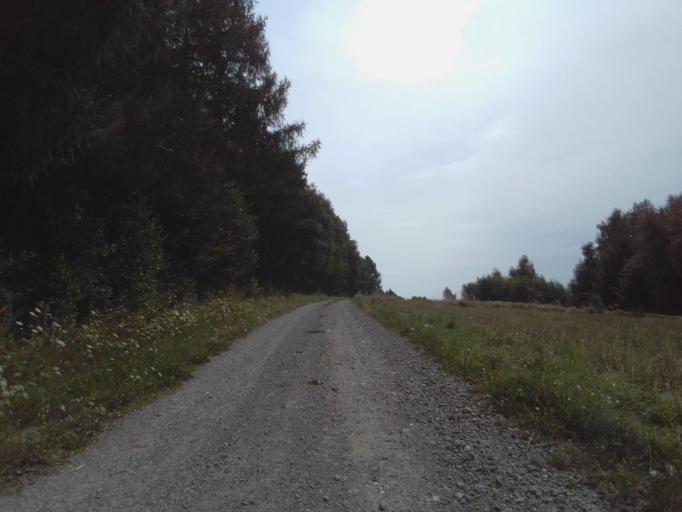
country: PL
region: Subcarpathian Voivodeship
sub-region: Powiat strzyzowski
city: Frysztak
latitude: 49.8663
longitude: 21.5742
